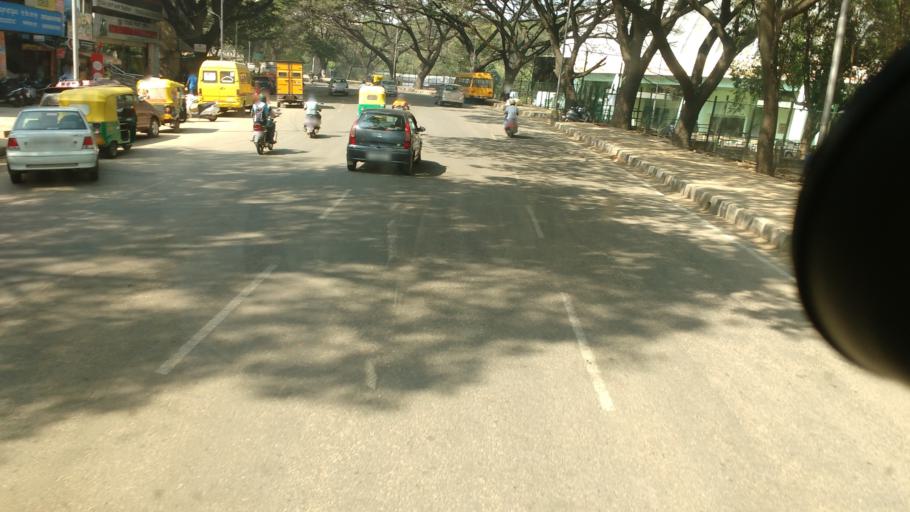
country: IN
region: Karnataka
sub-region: Bangalore Urban
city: Bangalore
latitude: 12.9681
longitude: 77.5923
